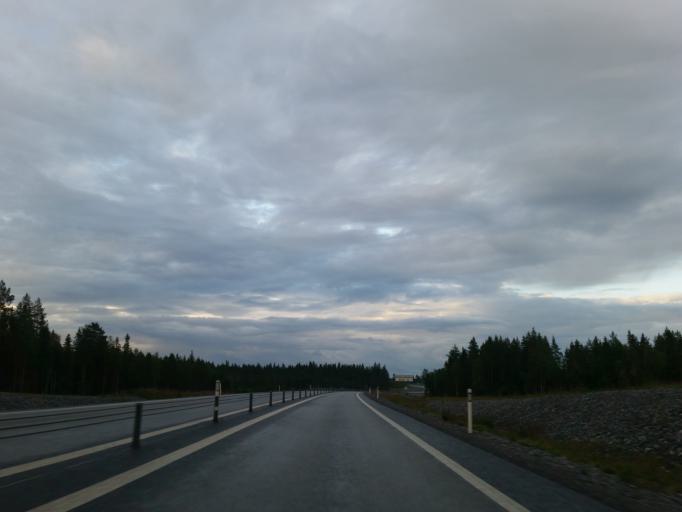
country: SE
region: Vaesterbotten
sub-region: Umea Kommun
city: Umea
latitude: 63.8579
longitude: 20.2460
